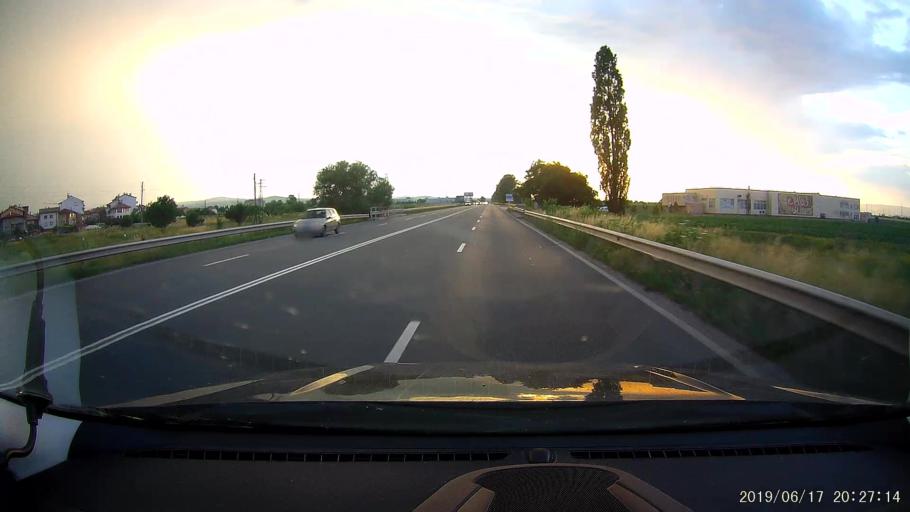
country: BG
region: Sofiya
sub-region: Obshtina Bozhurishte
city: Bozhurishte
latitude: 42.7703
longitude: 23.2001
